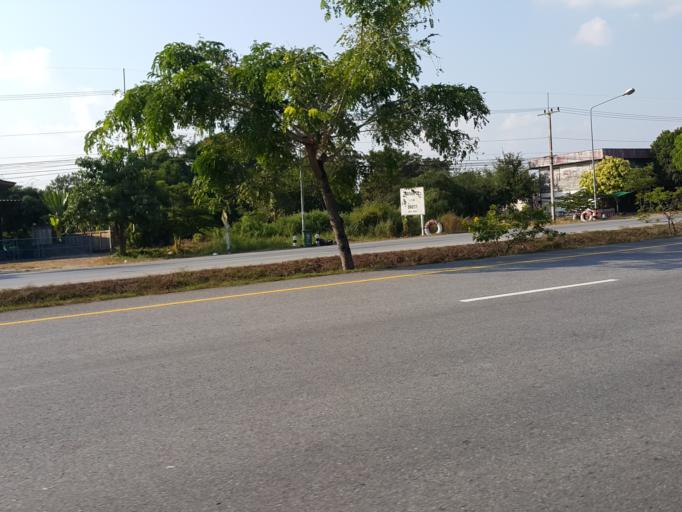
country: TH
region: Lampang
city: Thoen
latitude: 17.6343
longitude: 99.2392
